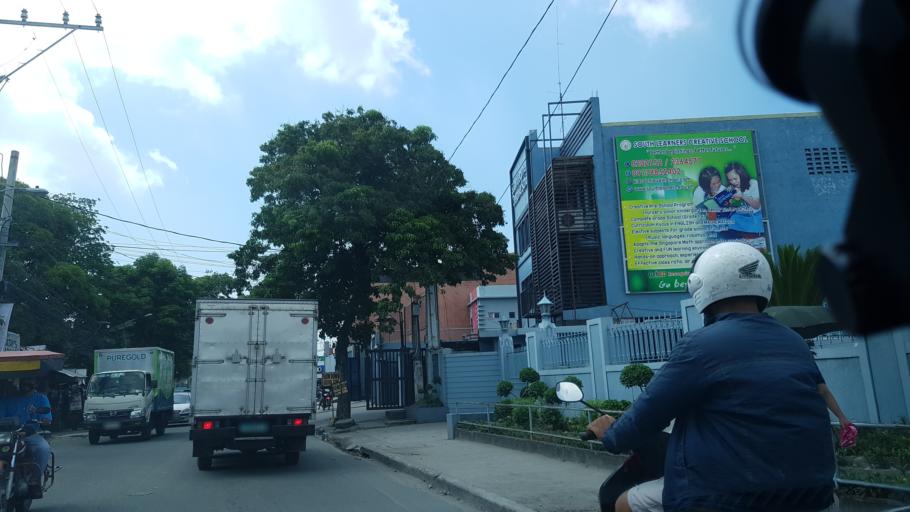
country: PH
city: Sambayanihan People's Village
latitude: 14.4616
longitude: 120.9927
